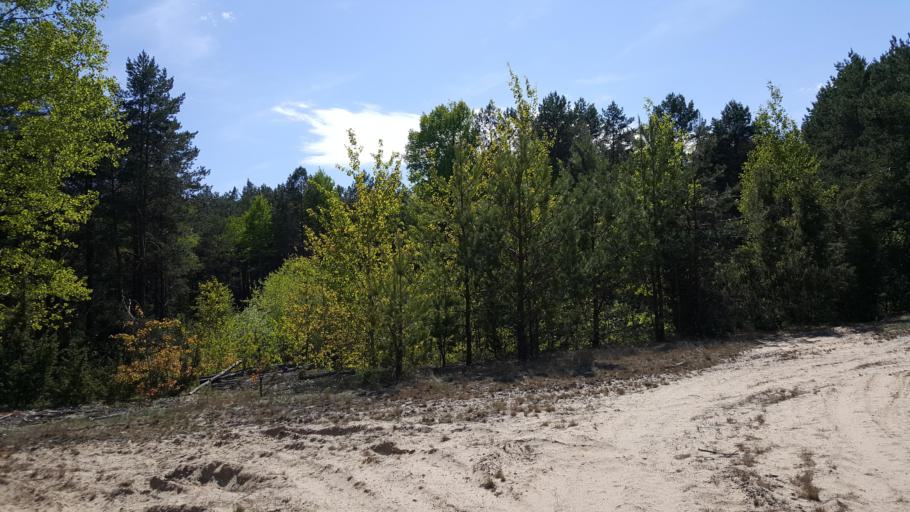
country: BY
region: Brest
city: Zhabinka
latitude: 52.3725
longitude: 24.1608
